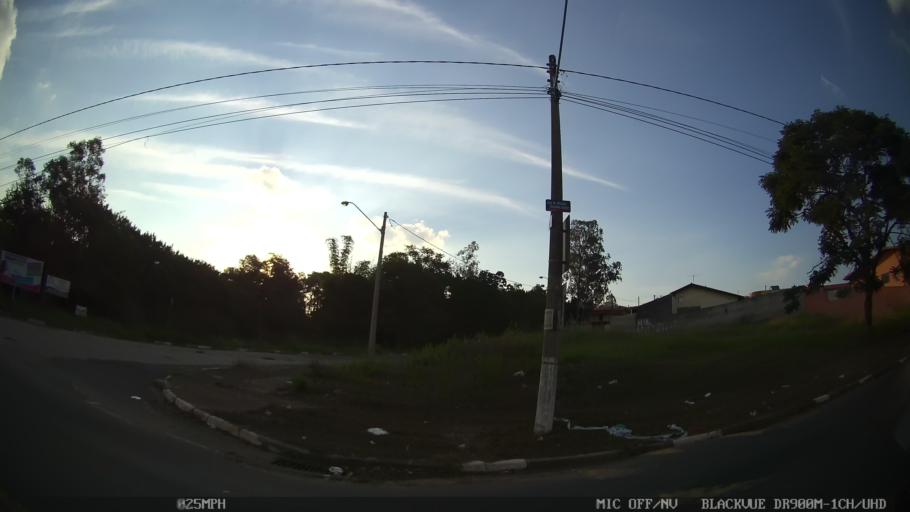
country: BR
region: Sao Paulo
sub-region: Hortolandia
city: Hortolandia
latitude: -22.8918
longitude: -47.1507
